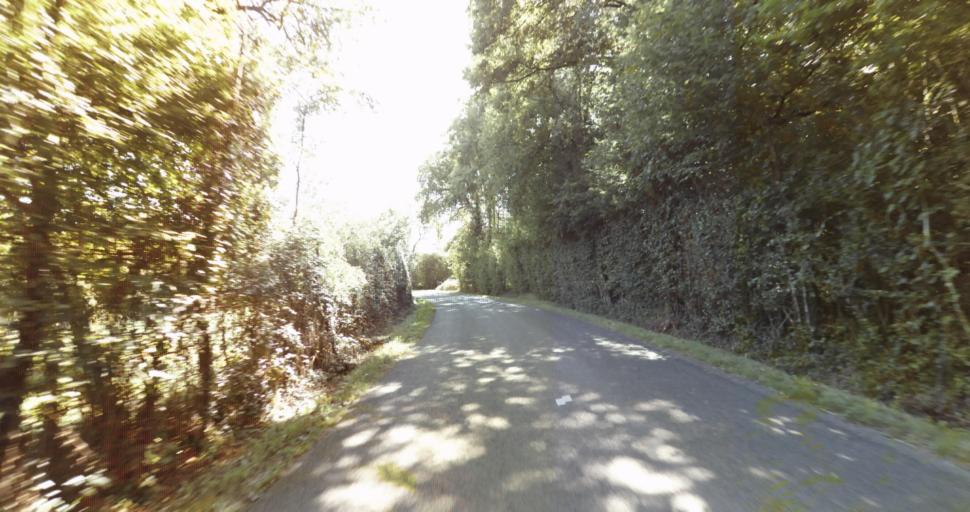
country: FR
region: Lower Normandy
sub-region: Departement de l'Orne
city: Gace
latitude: 48.7638
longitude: 0.2538
